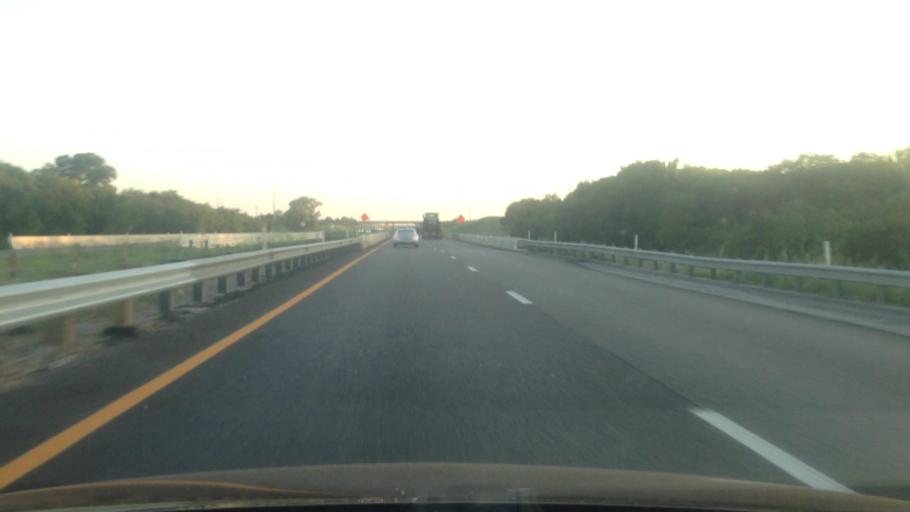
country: US
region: Texas
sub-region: Denton County
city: Argyle
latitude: 33.1770
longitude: -97.1781
